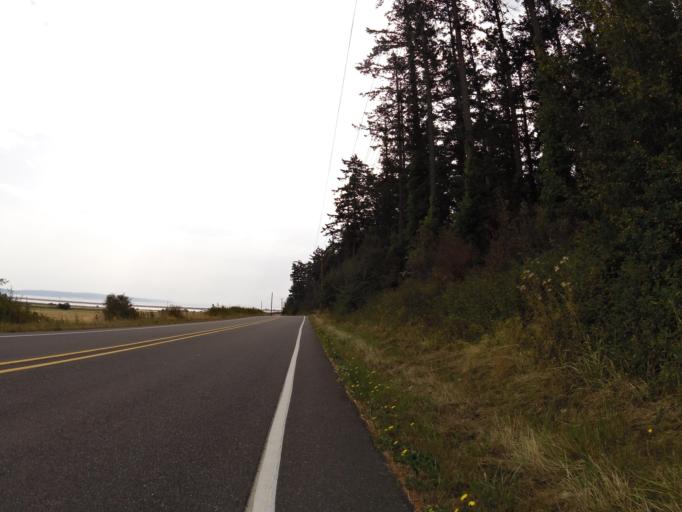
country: US
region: Washington
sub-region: Island County
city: Coupeville
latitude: 48.1831
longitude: -122.6693
